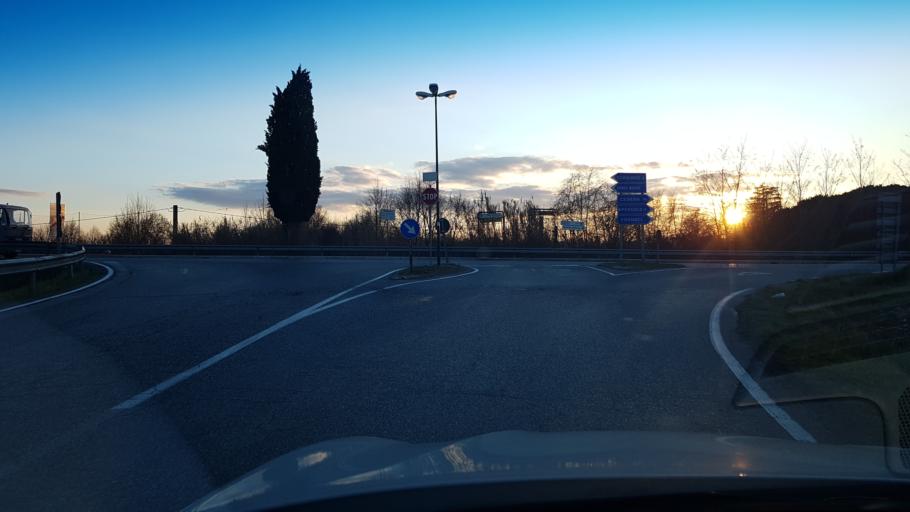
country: IT
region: Umbria
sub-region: Provincia di Perugia
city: Torgiano
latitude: 43.0120
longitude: 12.4280
